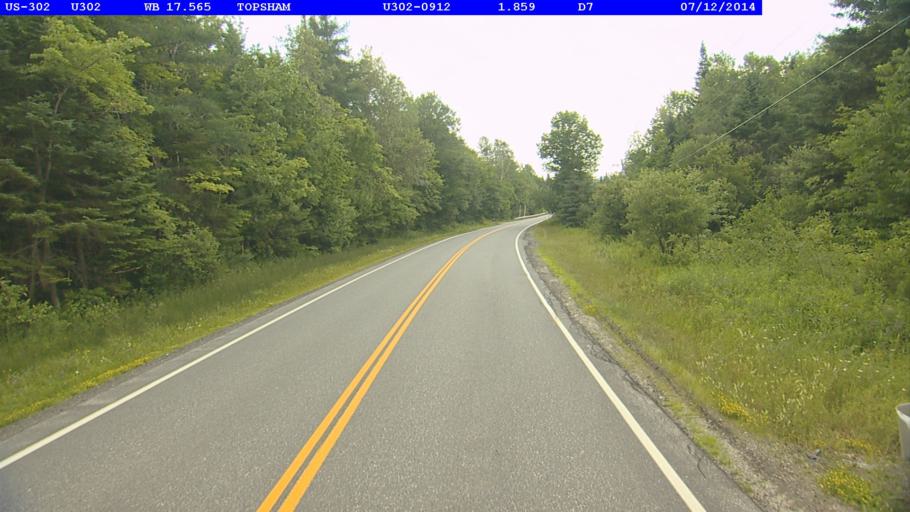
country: US
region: Vermont
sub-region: Washington County
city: Barre
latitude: 44.1629
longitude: -72.3064
